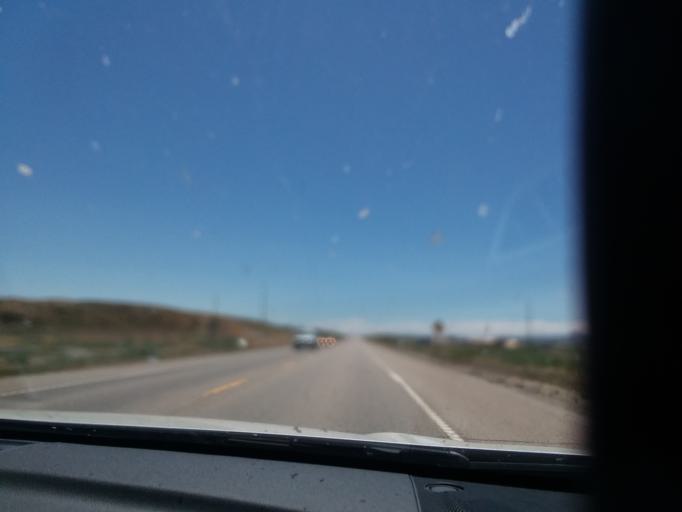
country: US
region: Wyoming
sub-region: Sweetwater County
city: North Rock Springs
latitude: 41.6364
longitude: -109.2299
